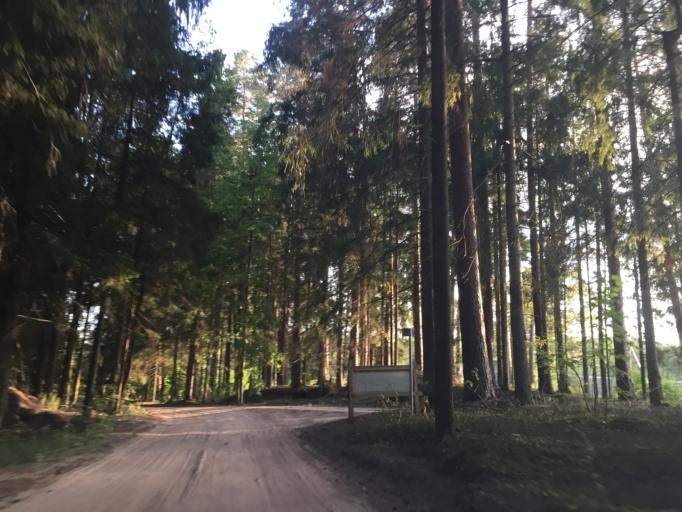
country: LV
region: Baldone
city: Baldone
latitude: 56.7593
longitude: 24.4089
